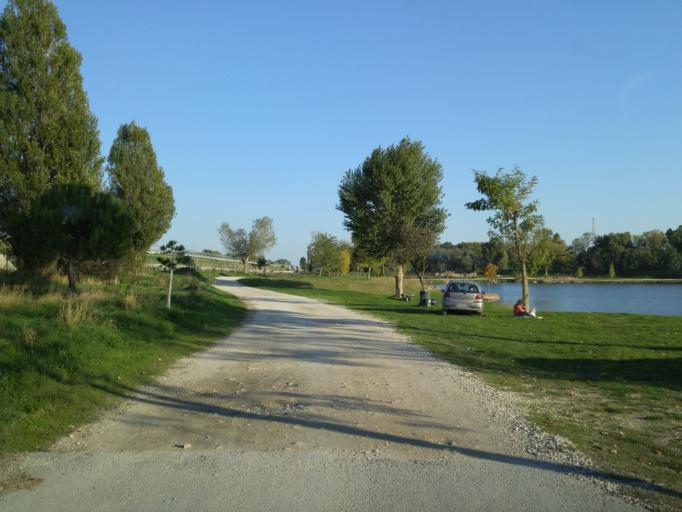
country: IT
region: The Marches
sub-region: Provincia di Pesaro e Urbino
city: Fano
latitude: 43.8126
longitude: 13.0336
